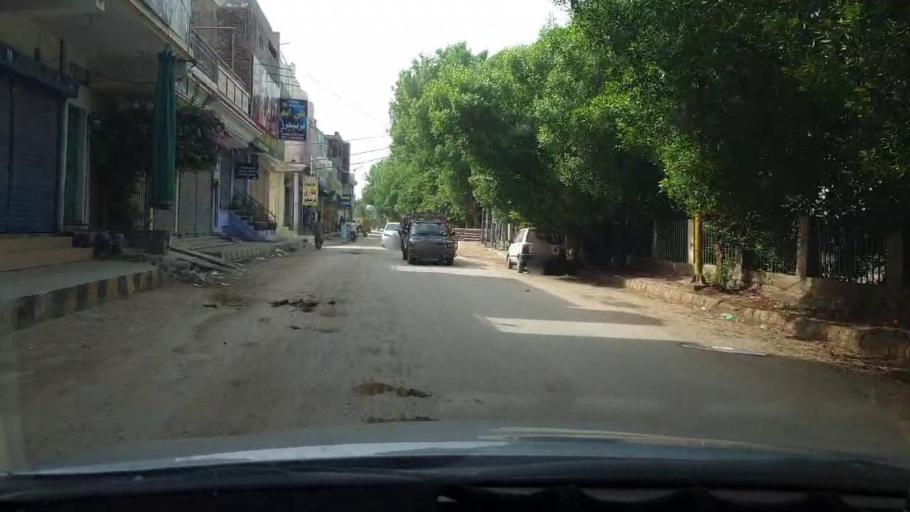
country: PK
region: Sindh
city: Khairpur
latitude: 27.5293
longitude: 68.7537
